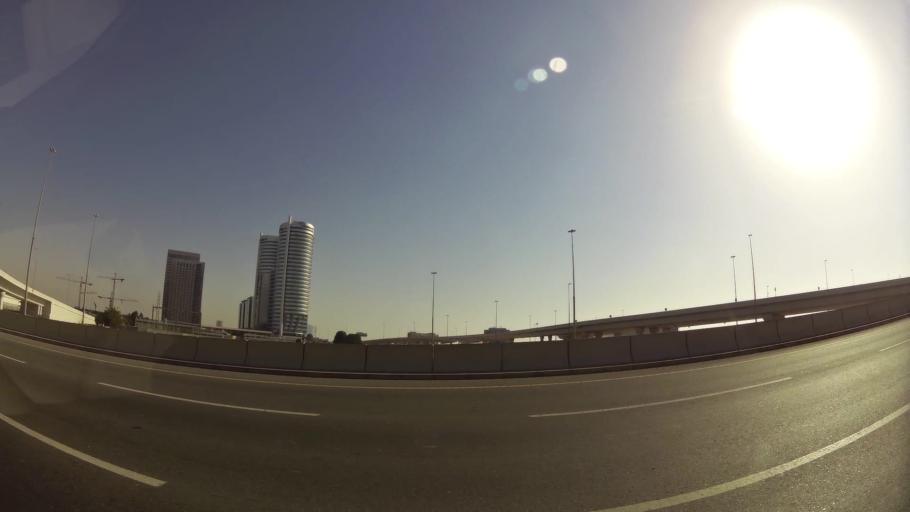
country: AE
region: Dubai
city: Dubai
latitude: 24.9877
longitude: 55.0960
